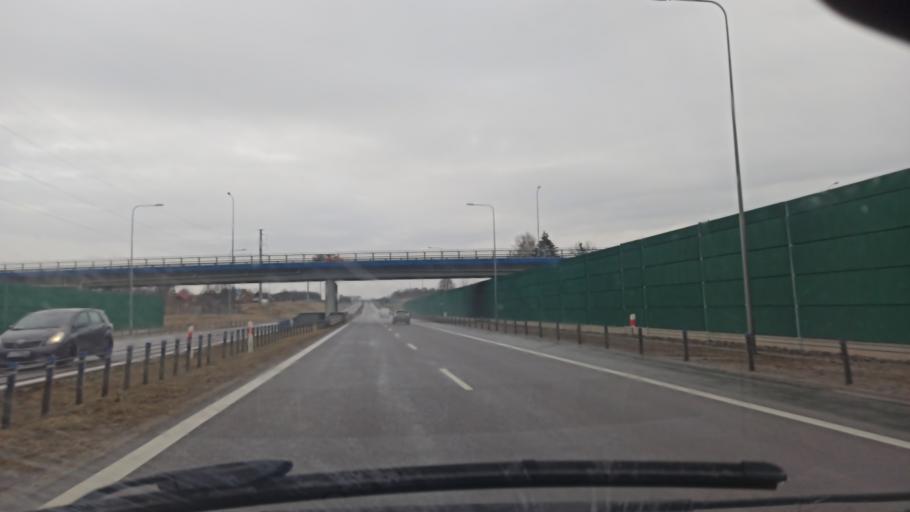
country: PL
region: Lublin Voivodeship
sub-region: Powiat lubelski
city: Kozubszczyzna
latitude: 51.2205
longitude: 22.4401
